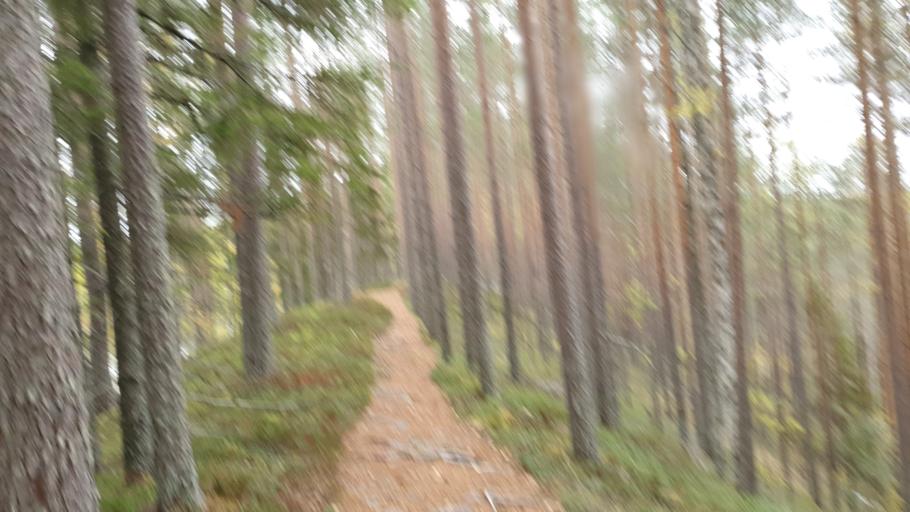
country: FI
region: Kainuu
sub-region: Kehys-Kainuu
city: Kuhmo
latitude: 64.2931
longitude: 29.3502
